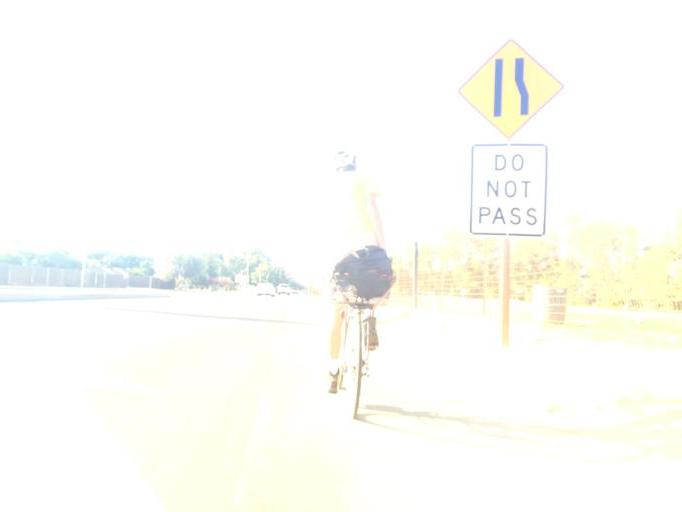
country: US
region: California
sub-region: Fresno County
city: Sunnyside
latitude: 36.7547
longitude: -119.6819
